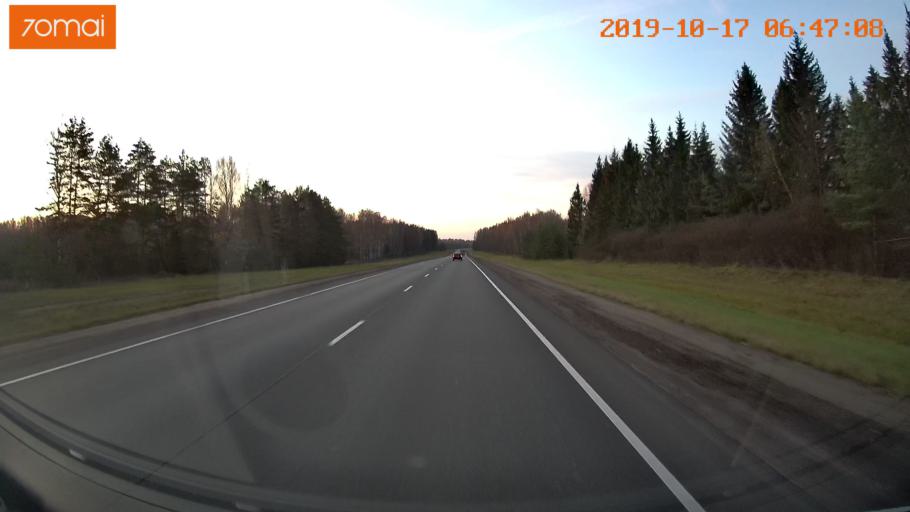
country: RU
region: Vladimir
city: Kideksha
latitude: 56.5402
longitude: 40.5554
